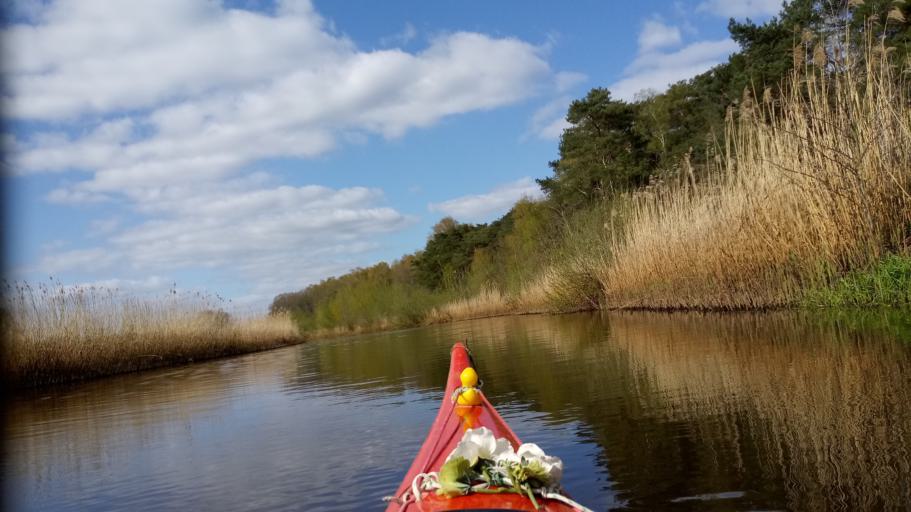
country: NL
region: Overijssel
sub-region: Gemeente Twenterand
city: Den Ham
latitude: 52.4736
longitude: 6.4541
